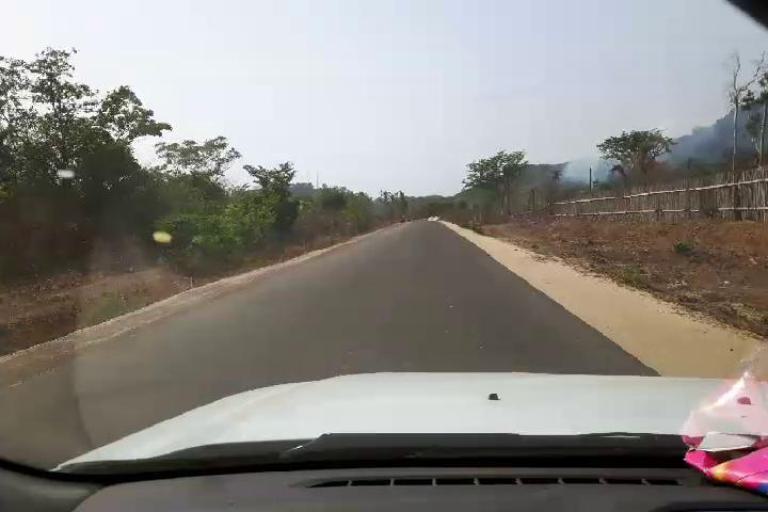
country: SL
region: Western Area
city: Waterloo
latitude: 8.2539
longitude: -13.1562
